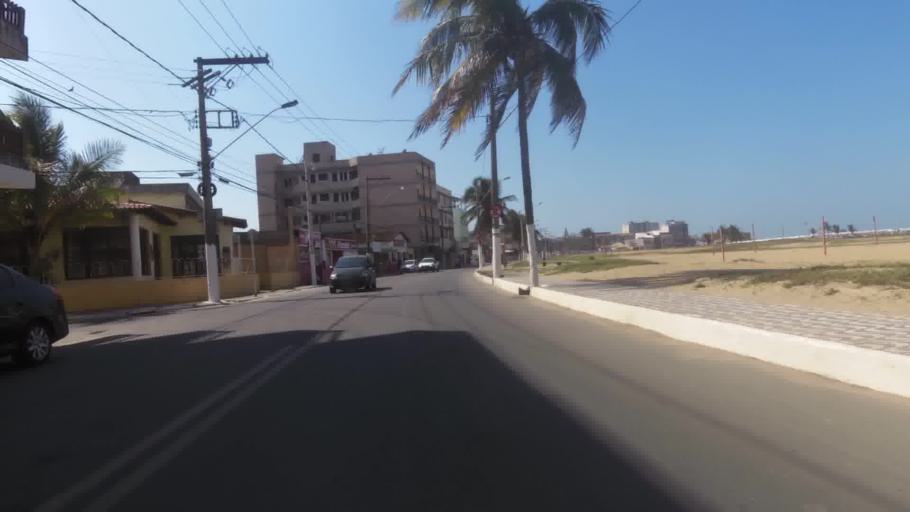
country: BR
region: Espirito Santo
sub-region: Marataizes
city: Marataizes
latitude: -21.0451
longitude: -40.8285
